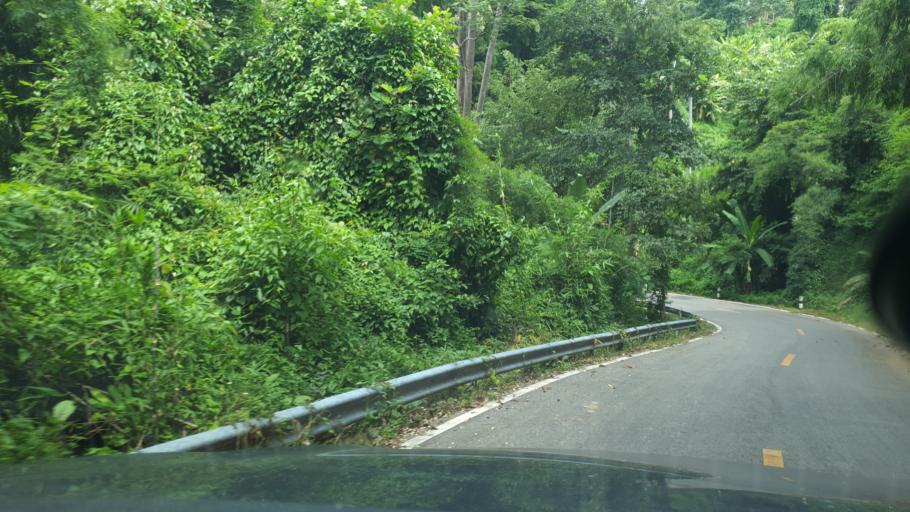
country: TH
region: Lamphun
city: Mae Tha
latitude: 18.4971
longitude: 99.2683
